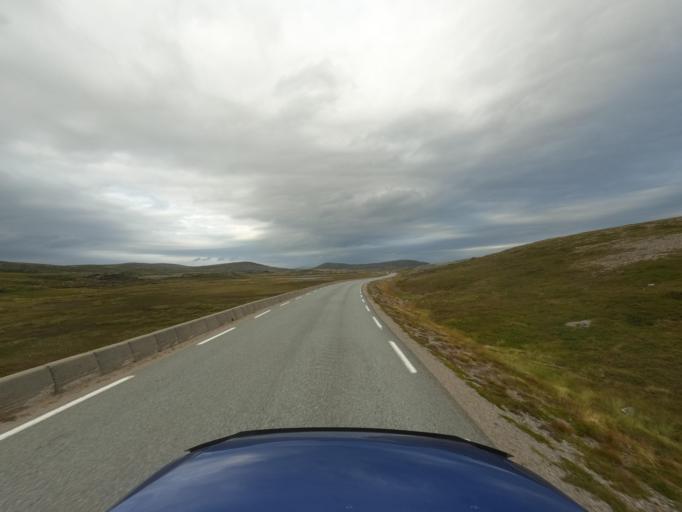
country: NO
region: Finnmark Fylke
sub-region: Nordkapp
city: Honningsvag
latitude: 70.8129
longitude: 25.7470
